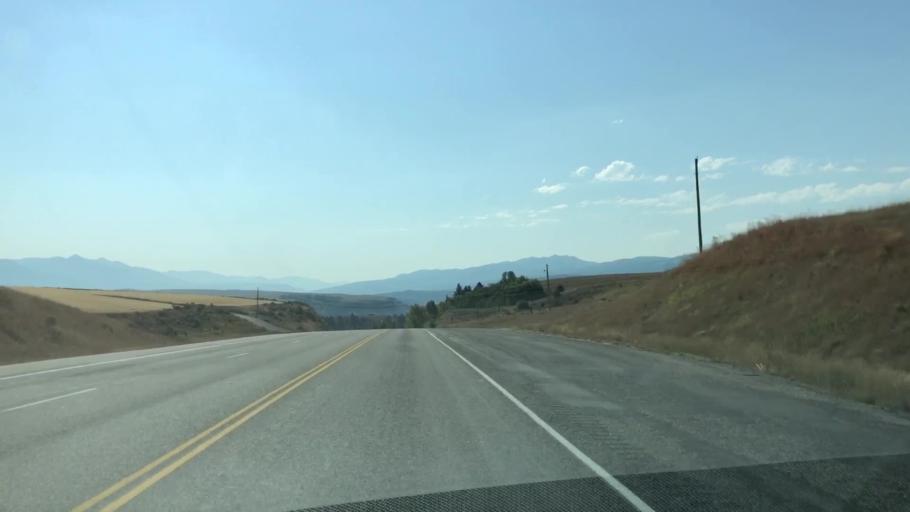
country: US
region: Idaho
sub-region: Teton County
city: Victor
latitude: 43.4935
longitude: -111.4563
